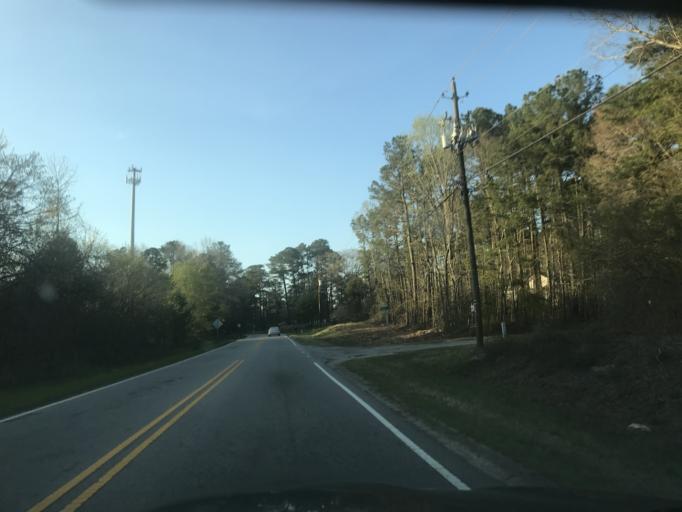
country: US
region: North Carolina
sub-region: Wake County
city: Knightdale
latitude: 35.7508
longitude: -78.5348
